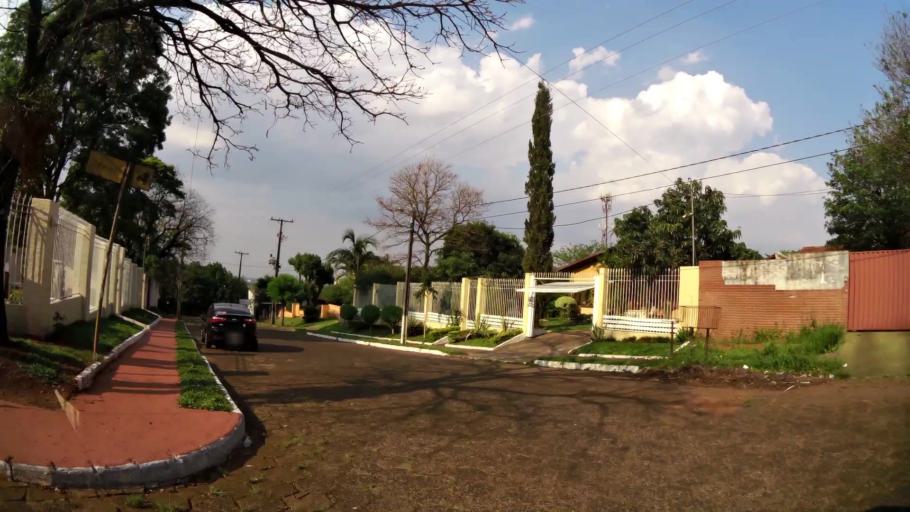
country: PY
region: Alto Parana
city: Presidente Franco
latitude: -25.5305
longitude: -54.6300
